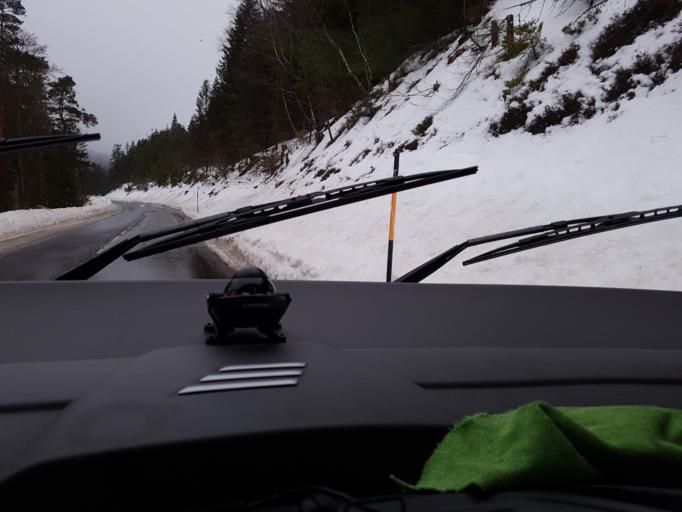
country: FR
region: Alsace
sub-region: Departement du Haut-Rhin
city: Soultzeren
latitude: 48.1264
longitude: 7.0943
